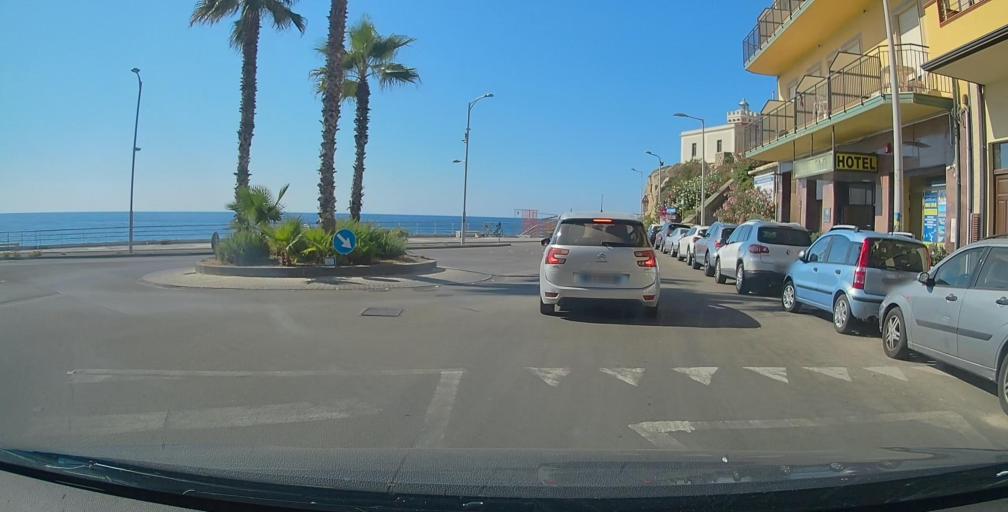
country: IT
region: Sicily
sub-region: Messina
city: Capo d'Orlando
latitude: 38.1639
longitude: 14.7470
